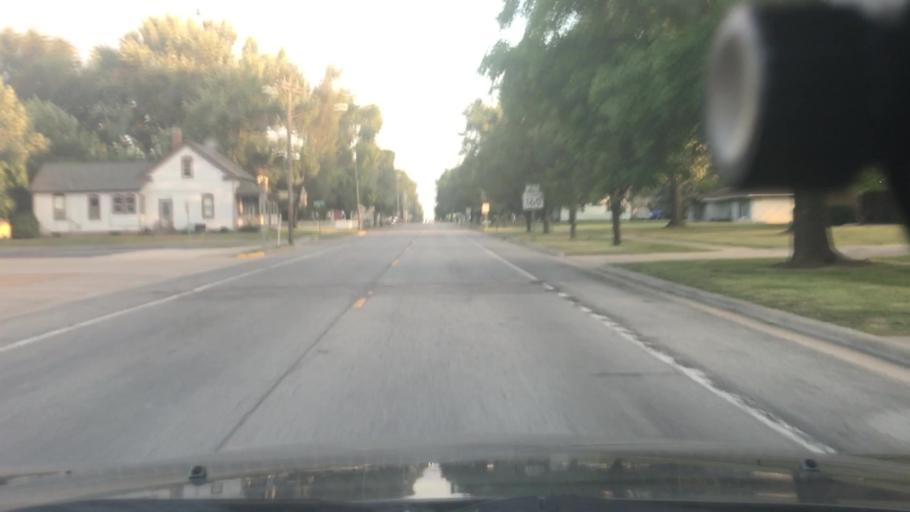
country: US
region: Illinois
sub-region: Washington County
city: Okawville
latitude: 38.4327
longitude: -89.5506
